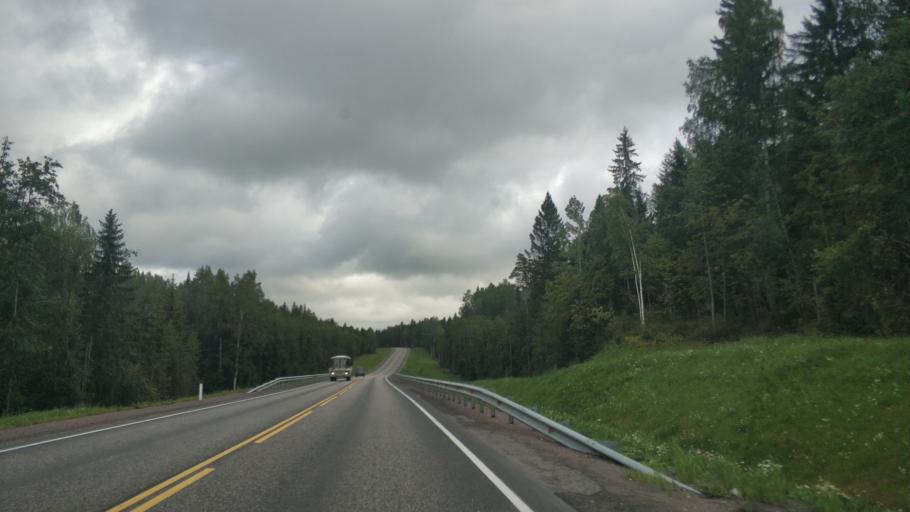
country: RU
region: Republic of Karelia
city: Khelyulya
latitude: 61.8348
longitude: 30.6408
